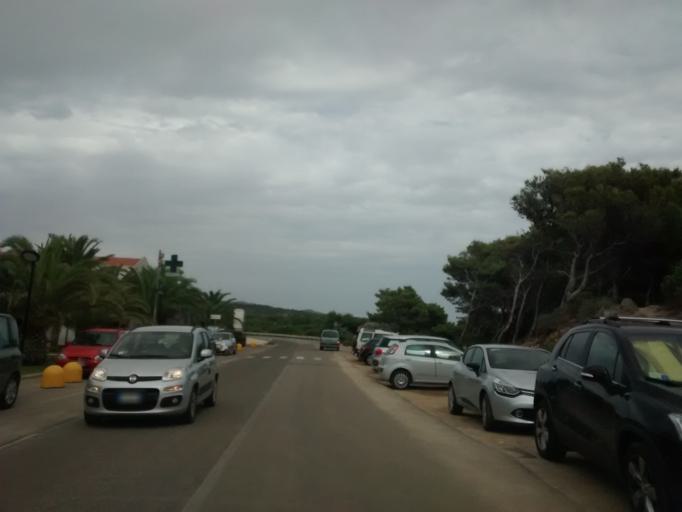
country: IT
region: Sardinia
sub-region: Provincia di Cagliari
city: Villasimius
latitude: 39.1169
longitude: 9.5086
